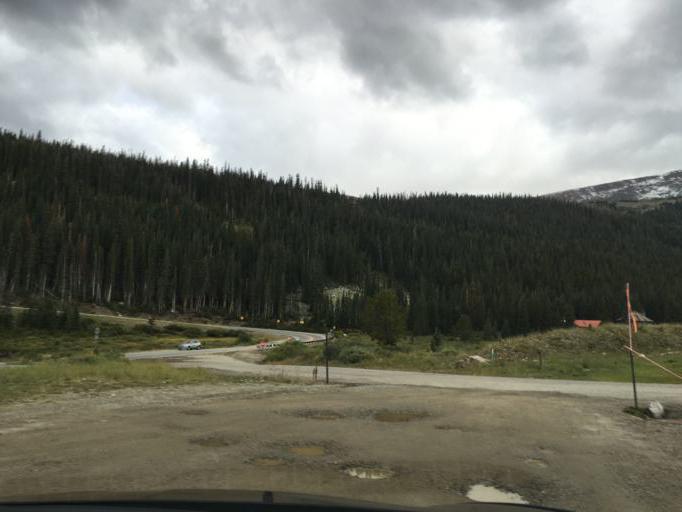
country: US
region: Colorado
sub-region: Summit County
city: Breckenridge
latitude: 39.3821
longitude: -106.0631
